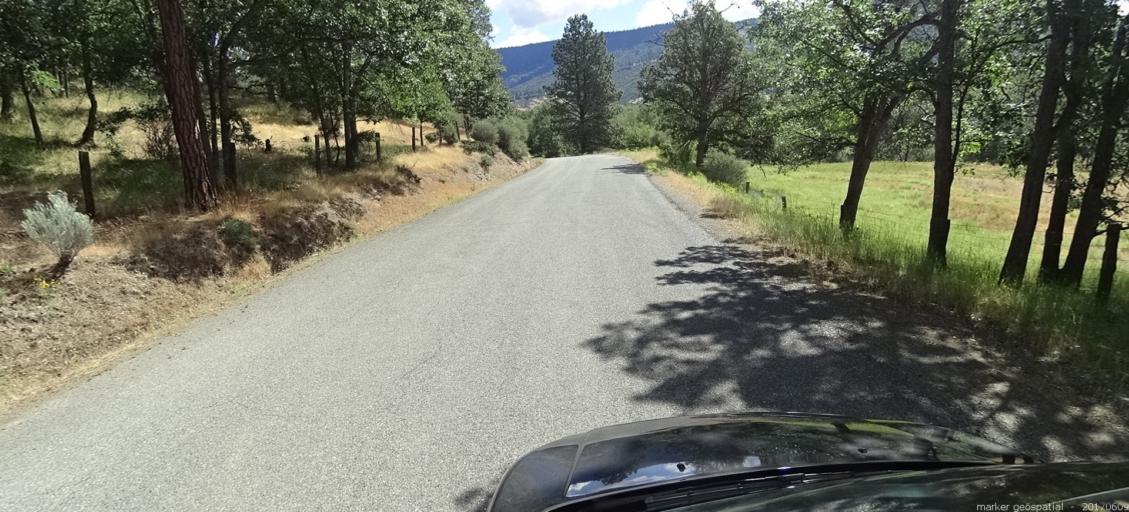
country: US
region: California
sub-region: Siskiyou County
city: Yreka
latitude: 41.3338
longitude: -122.8315
